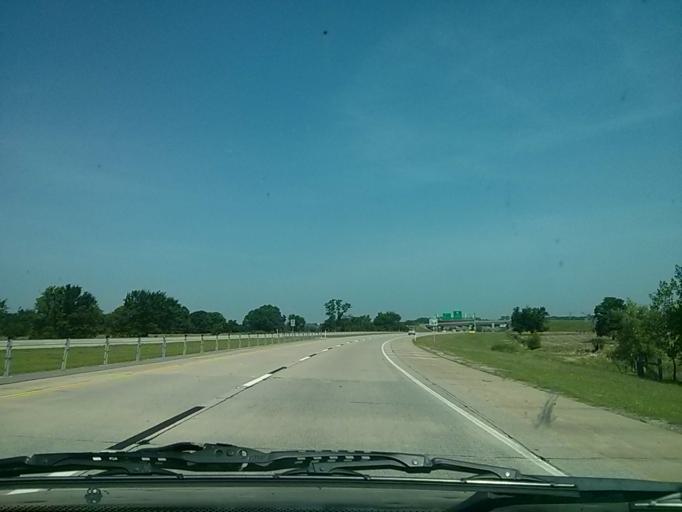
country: US
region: Oklahoma
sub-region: Creek County
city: Sapulpa
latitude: 36.0217
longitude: -96.0725
